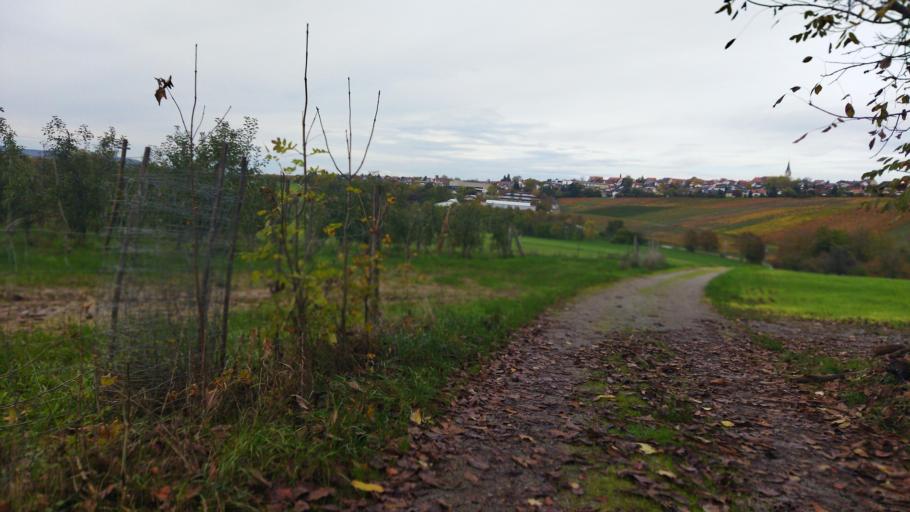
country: DE
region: Baden-Wuerttemberg
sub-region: Regierungsbezirk Stuttgart
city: Neckarwestheim
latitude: 49.0372
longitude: 9.1874
